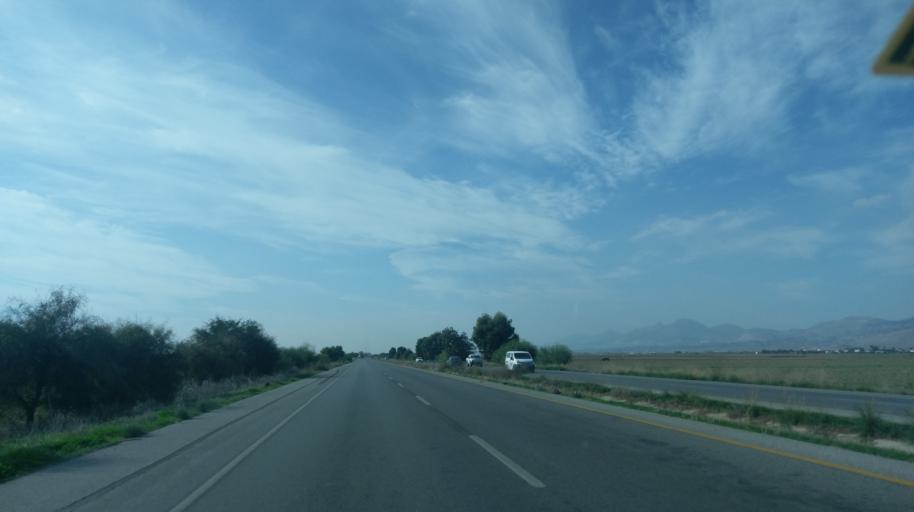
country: CY
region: Larnaka
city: Athienou
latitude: 35.2096
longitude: 33.5712
